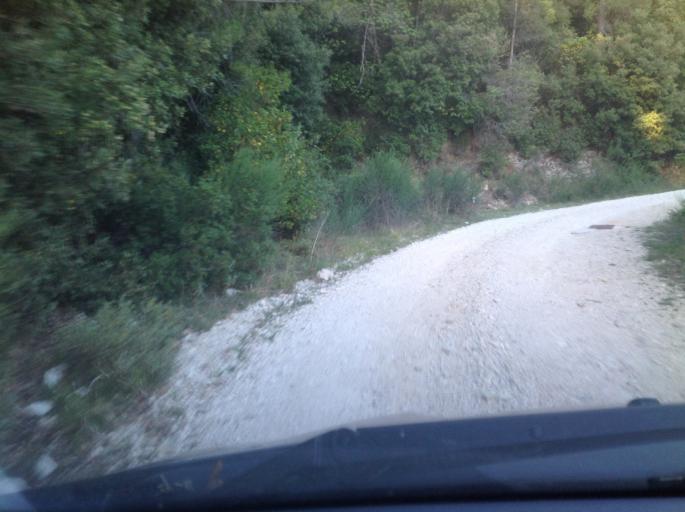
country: IT
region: Umbria
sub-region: Provincia di Terni
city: Stroncone
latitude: 42.5067
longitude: 12.6746
